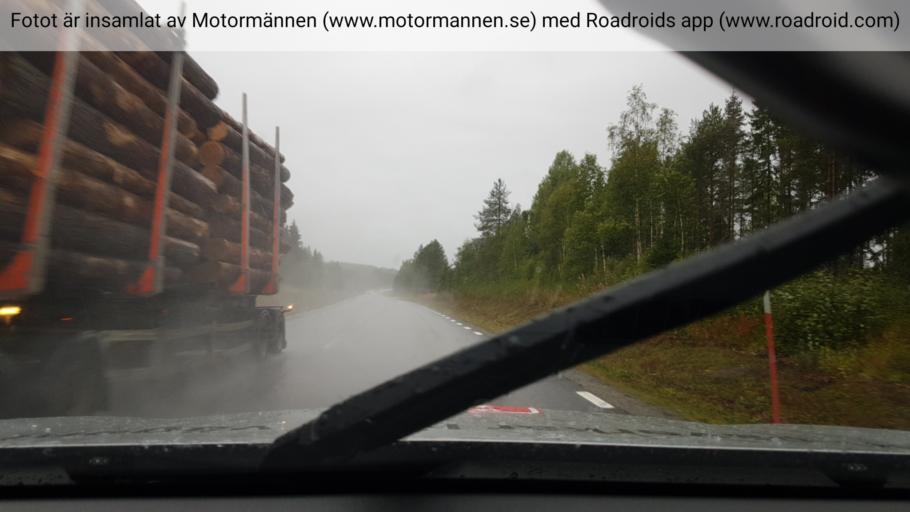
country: SE
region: Vaesterbotten
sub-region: Vannas Kommun
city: Vaennaes
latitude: 63.9142
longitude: 19.6498
